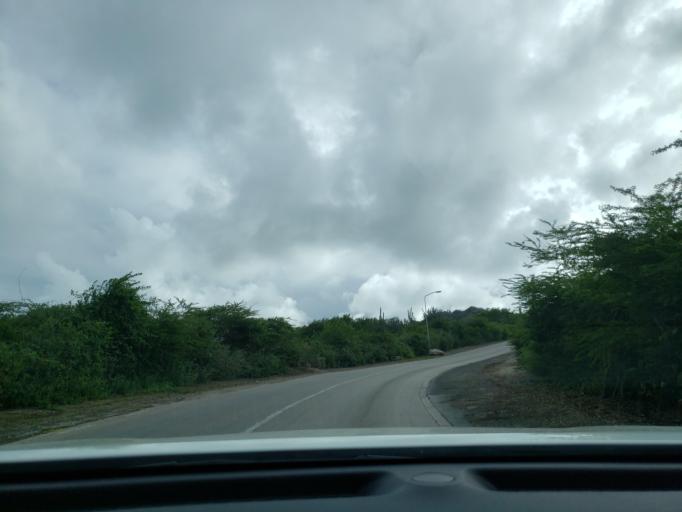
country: CW
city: Dorp Soto
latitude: 12.2127
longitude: -69.0716
